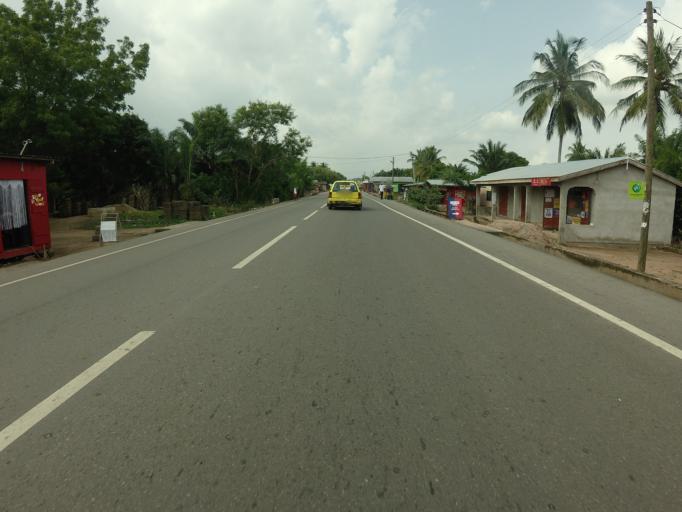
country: GH
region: Volta
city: Ho
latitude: 6.6237
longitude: 0.4821
